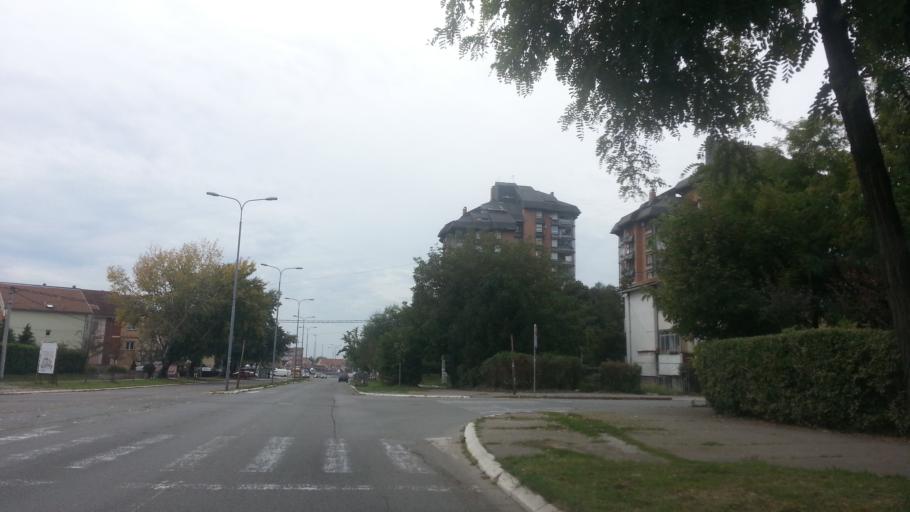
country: RS
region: Central Serbia
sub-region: Belgrade
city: Zemun
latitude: 44.8559
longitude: 20.3713
